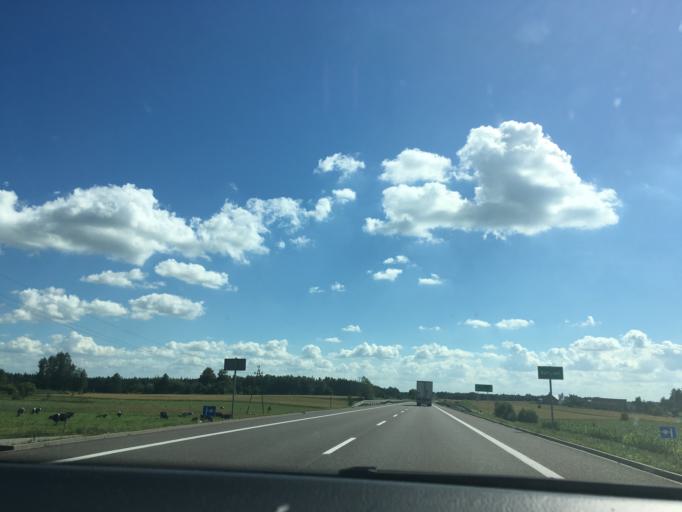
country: PL
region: Podlasie
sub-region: Powiat sokolski
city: Suchowola
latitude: 53.7072
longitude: 23.0977
